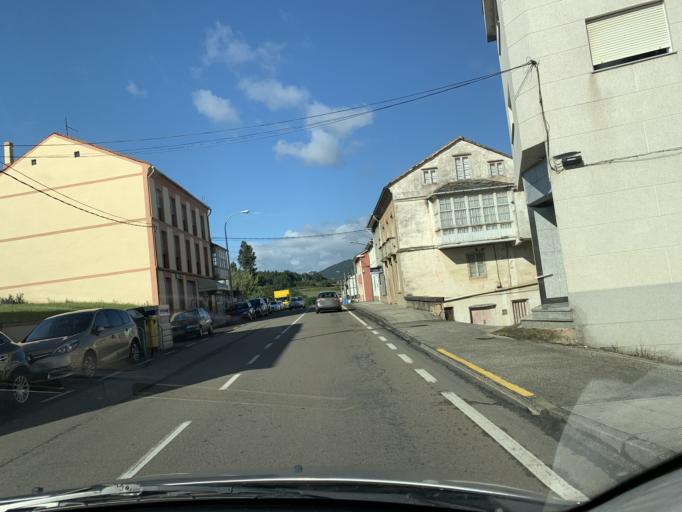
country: ES
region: Galicia
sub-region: Provincia de Lugo
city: Barreiros
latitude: 43.5406
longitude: -7.2340
